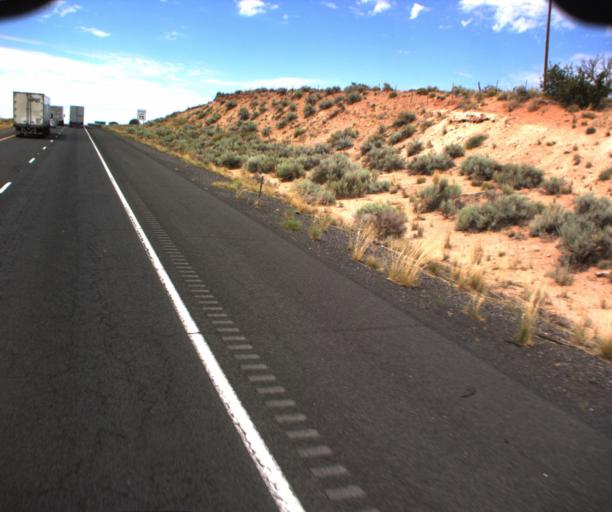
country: US
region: Arizona
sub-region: Apache County
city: Houck
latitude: 35.1595
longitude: -109.4941
